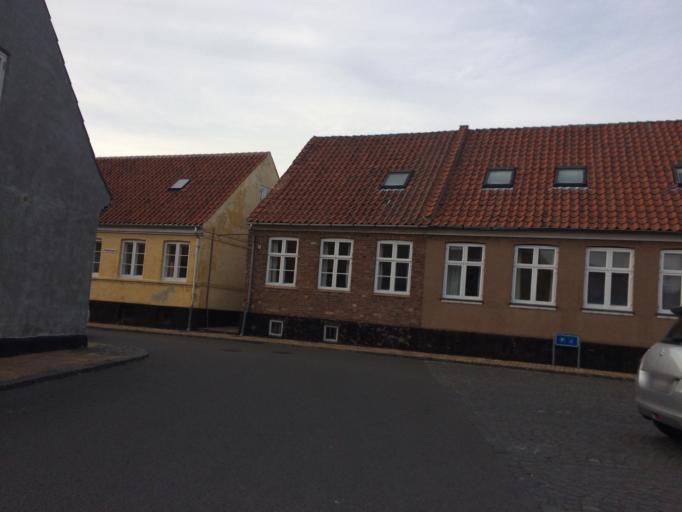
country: DK
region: Capital Region
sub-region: Bornholm Kommune
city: Ronne
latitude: 55.1025
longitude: 14.7027
